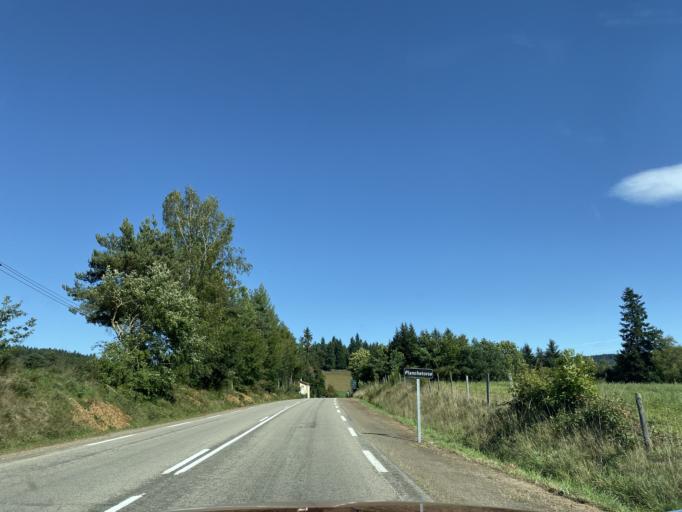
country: FR
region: Rhone-Alpes
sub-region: Departement de la Loire
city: Saint-Just-en-Chevalet
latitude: 45.8904
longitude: 3.8433
